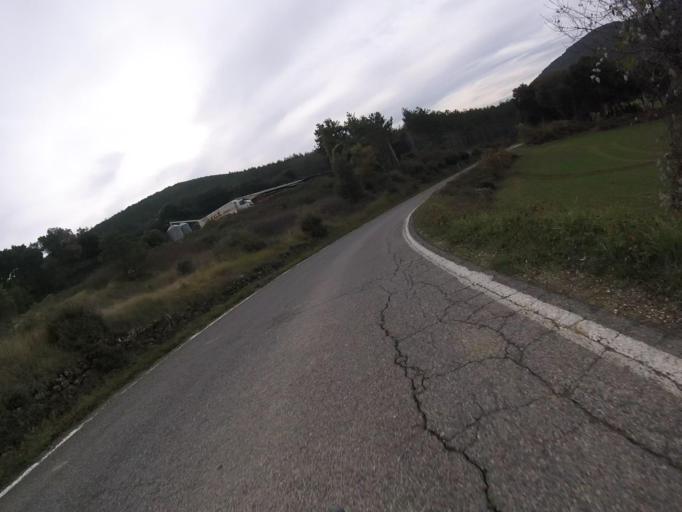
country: ES
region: Navarre
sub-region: Provincia de Navarra
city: Estella
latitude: 42.7115
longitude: -2.0453
